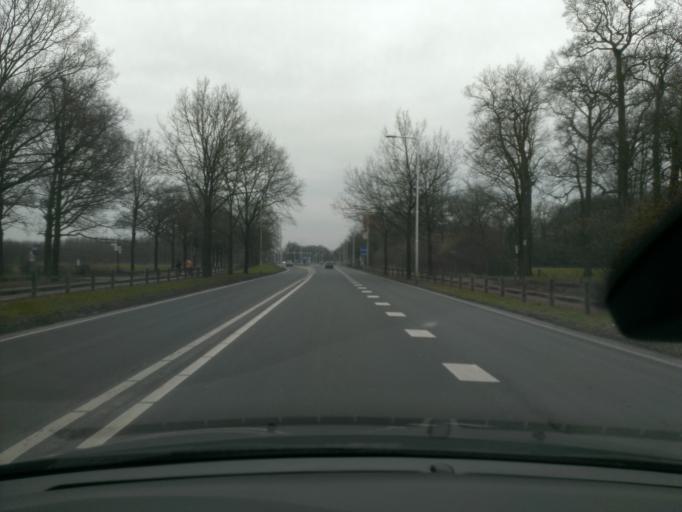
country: NL
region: Overijssel
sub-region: Gemeente Almelo
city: Almelo
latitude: 52.3590
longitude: 6.6736
